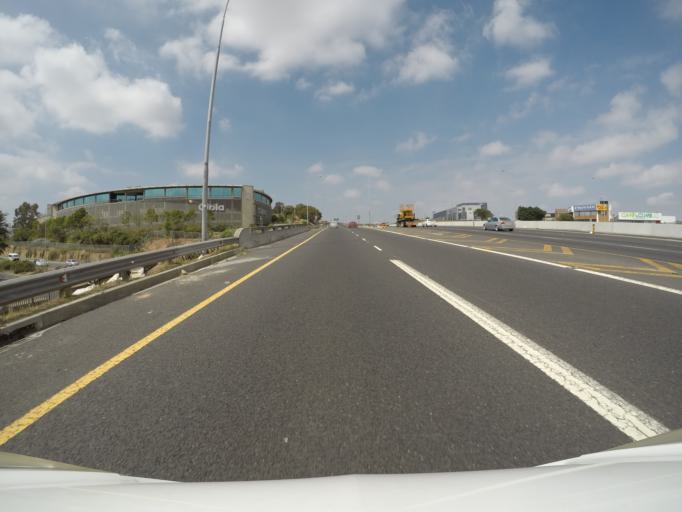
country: ZA
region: Western Cape
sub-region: City of Cape Town
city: Kraaifontein
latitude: -33.8876
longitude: 18.6301
